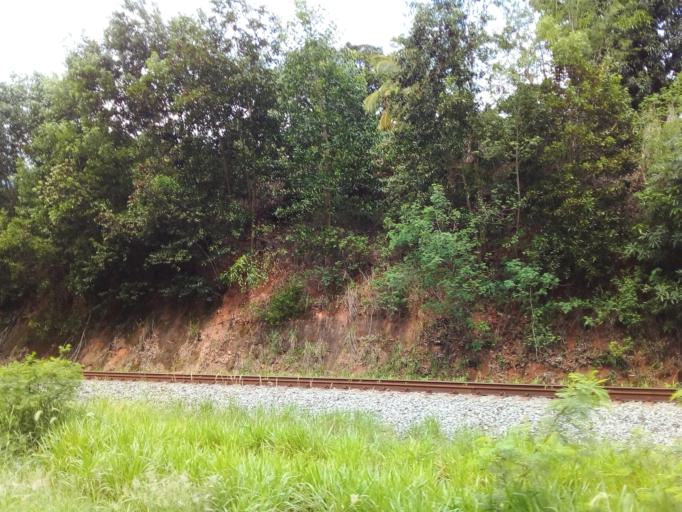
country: BR
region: Espirito Santo
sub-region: Joao Neiva
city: Joao Neiva
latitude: -19.7635
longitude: -40.3688
